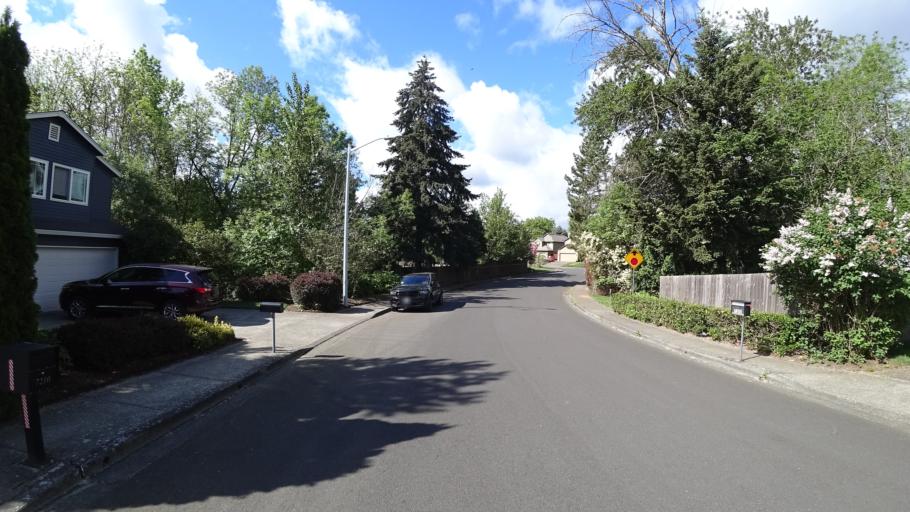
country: US
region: Oregon
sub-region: Washington County
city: Aloha
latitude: 45.4673
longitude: -122.8382
